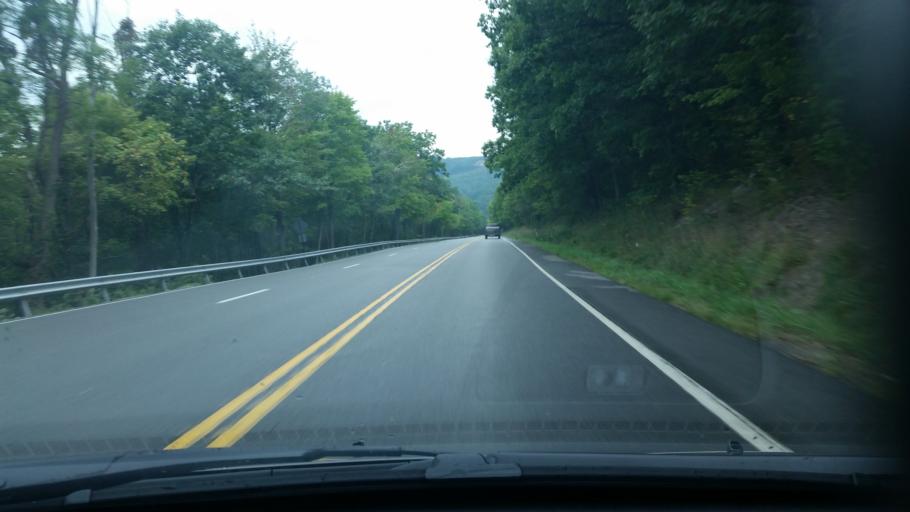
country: US
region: Pennsylvania
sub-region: Clearfield County
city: Shiloh
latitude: 41.0654
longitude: -78.3190
